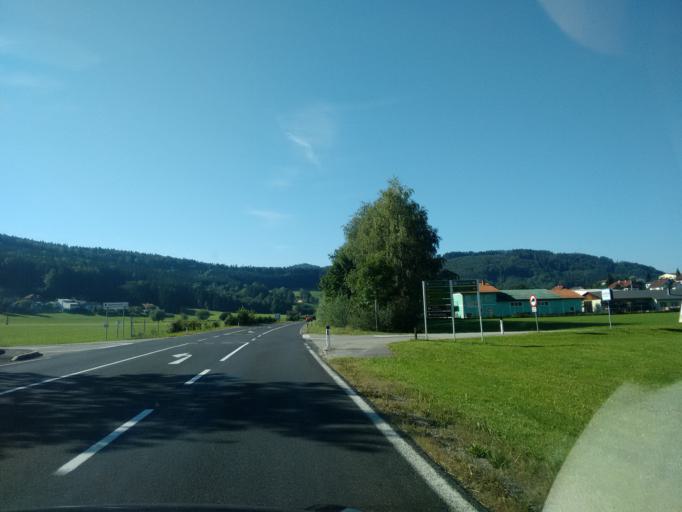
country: AT
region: Upper Austria
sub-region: Politischer Bezirk Vocklabruck
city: Seewalchen
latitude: 47.9442
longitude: 13.6112
